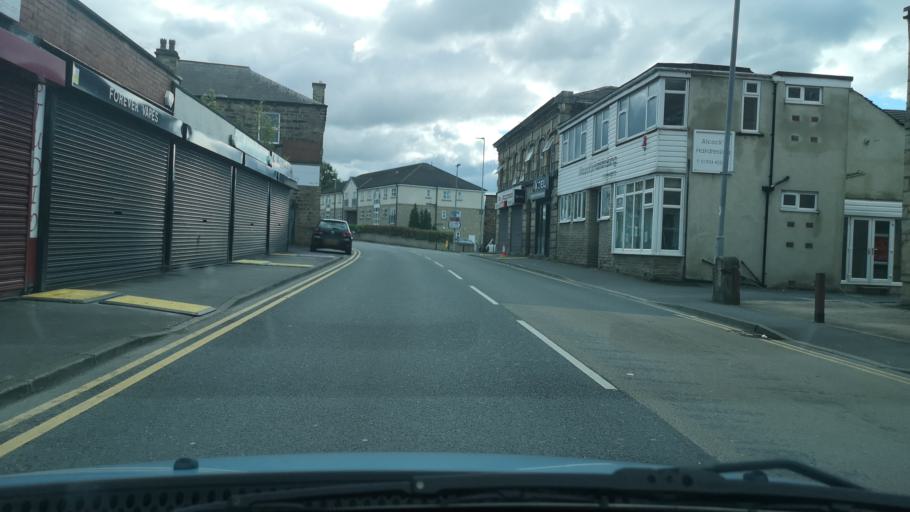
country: GB
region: England
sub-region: Kirklees
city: Heckmondwike
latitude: 53.7059
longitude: -1.6741
